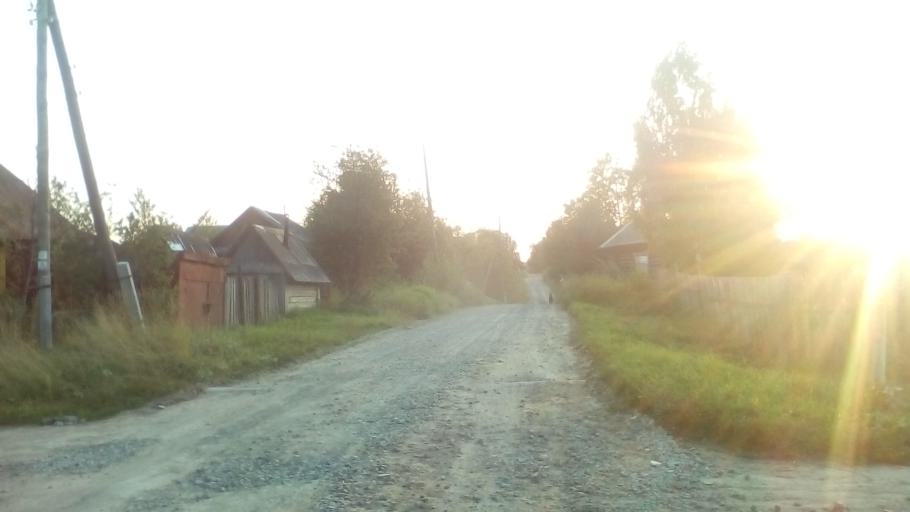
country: RU
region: Perm
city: Usol'ye
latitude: 59.4820
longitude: 56.5864
